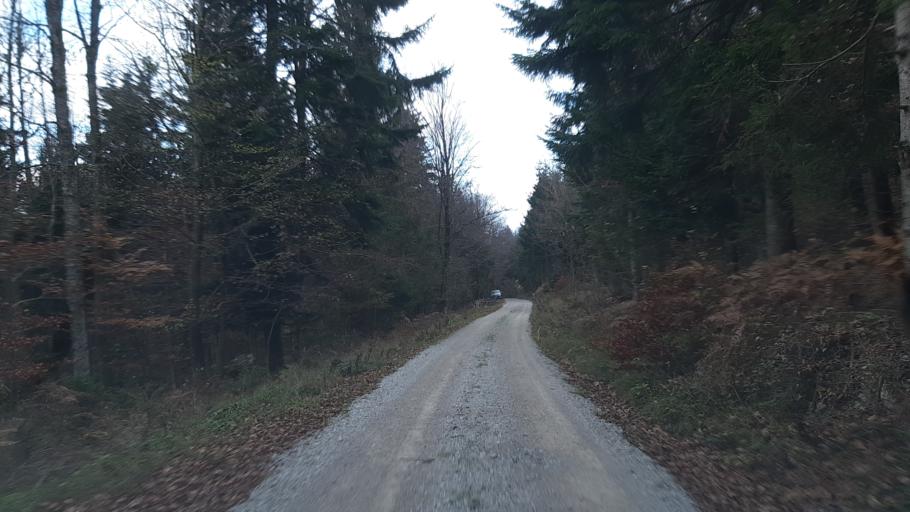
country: SI
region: Borovnica
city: Borovnica
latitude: 45.9321
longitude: 14.3812
